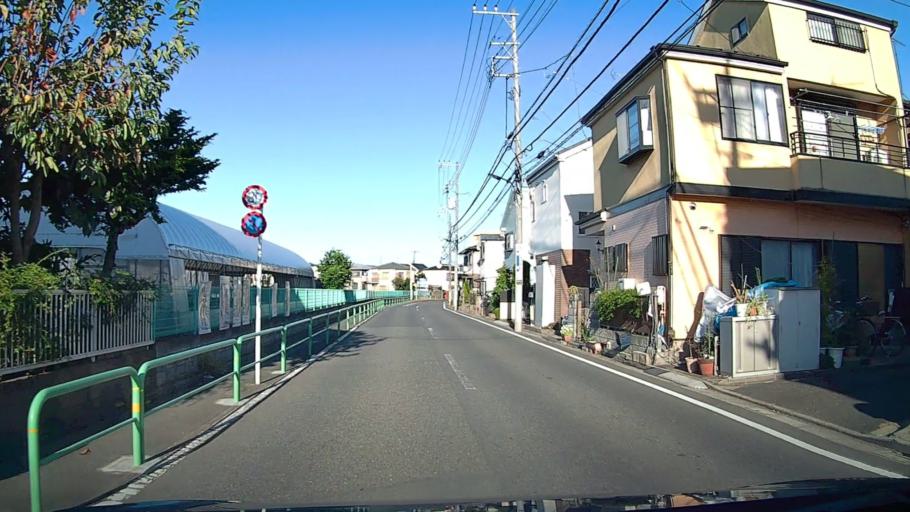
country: JP
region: Tokyo
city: Nishi-Tokyo-shi
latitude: 35.7556
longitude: 139.5711
